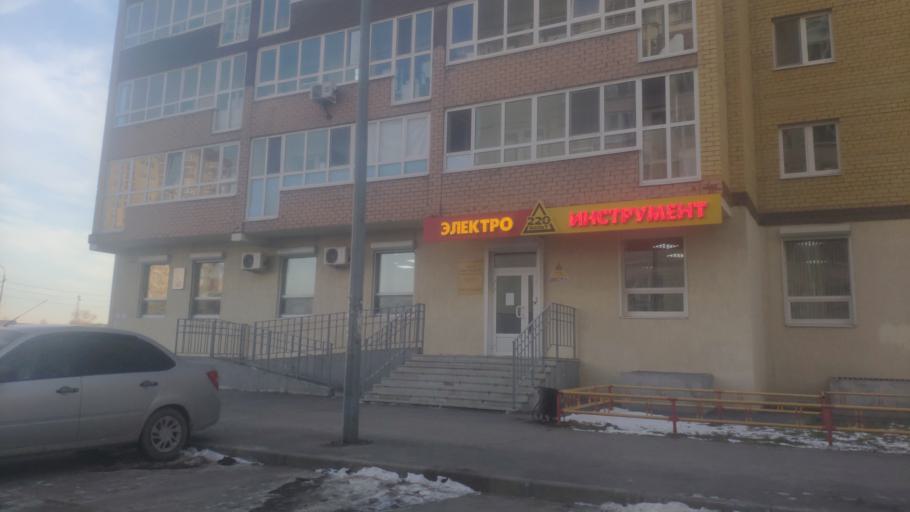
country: RU
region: Tjumen
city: Tyumen
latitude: 57.1776
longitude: 65.5674
